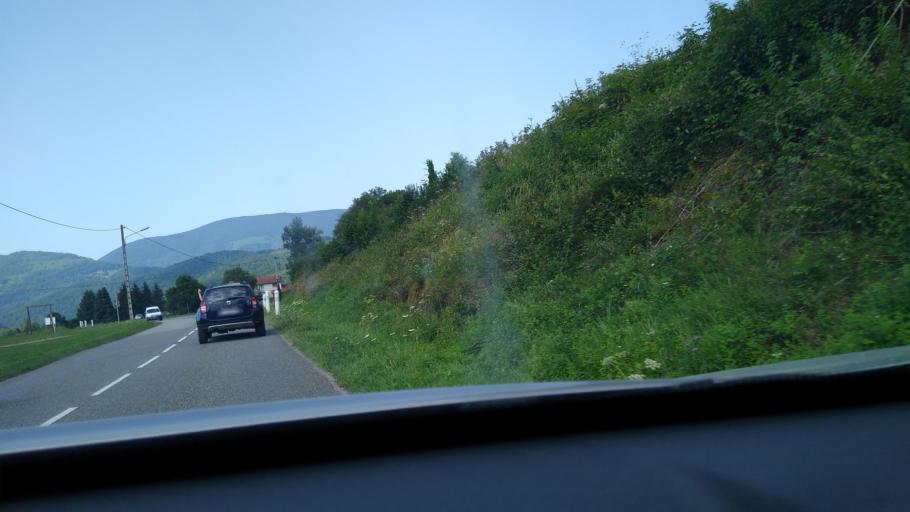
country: FR
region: Midi-Pyrenees
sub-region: Departement de l'Ariege
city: Saint-Girons
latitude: 42.8716
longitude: 1.2112
